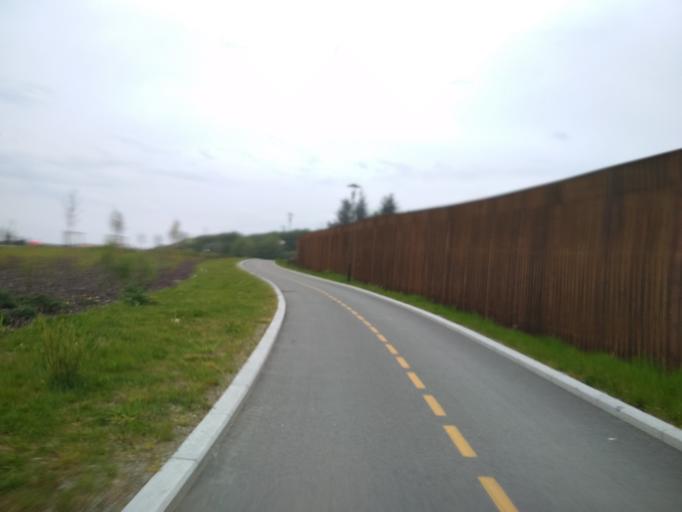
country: NO
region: Rogaland
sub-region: Stavanger
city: Stavanger
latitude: 58.9545
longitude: 5.7204
